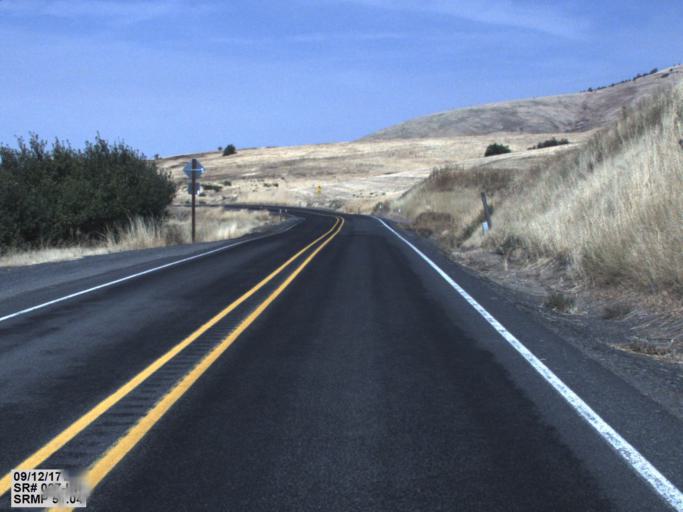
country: US
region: Idaho
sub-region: Benewah County
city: Plummer
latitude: 47.2374
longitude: -117.1194
